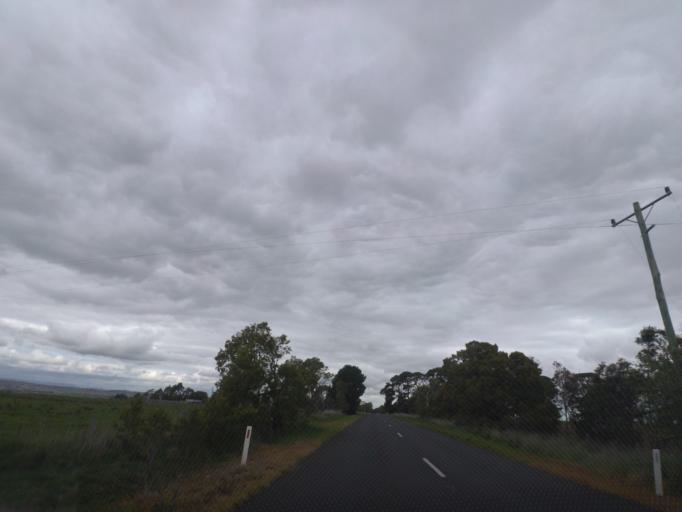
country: AU
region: Victoria
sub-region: Hume
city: Sunbury
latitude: -37.3886
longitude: 144.8314
